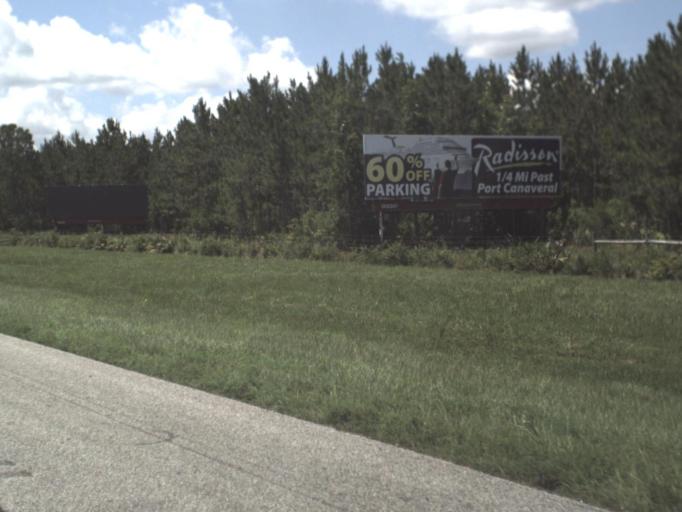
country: US
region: Florida
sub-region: Saint Johns County
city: Saint Augustine Shores
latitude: 29.7864
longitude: -81.3621
